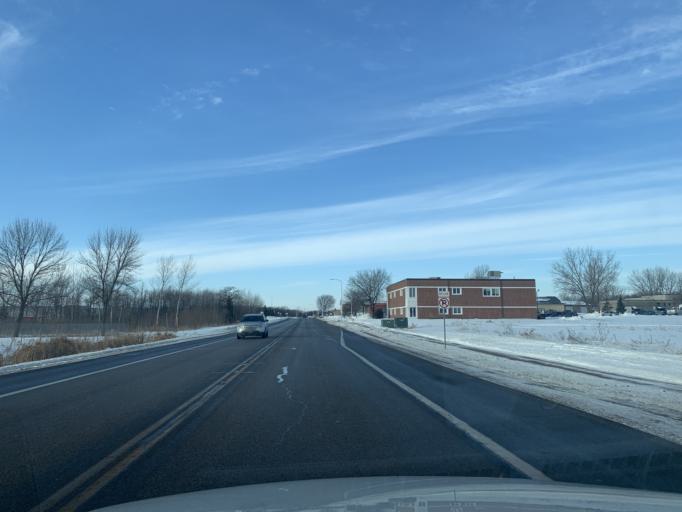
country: US
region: Minnesota
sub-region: Wright County
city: Buffalo
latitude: 45.1656
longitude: -93.8515
